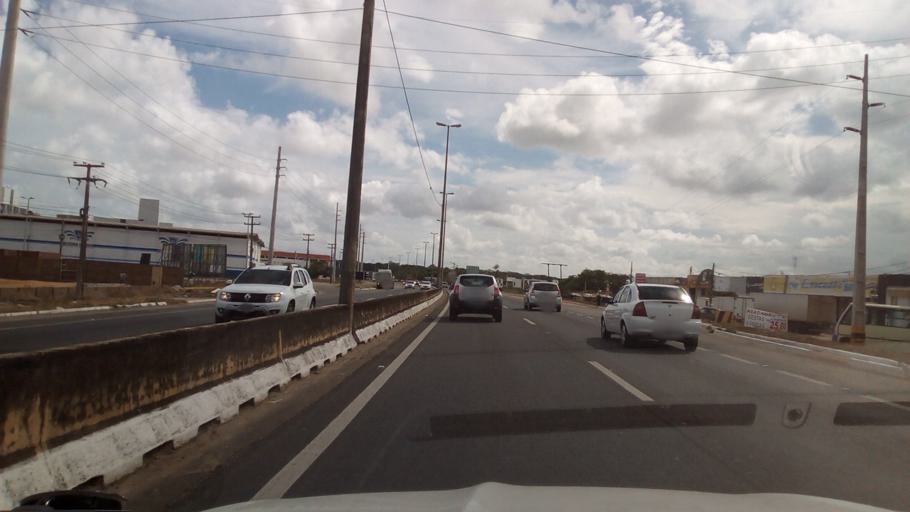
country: BR
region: Paraiba
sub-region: Joao Pessoa
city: Joao Pessoa
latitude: -7.0502
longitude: -34.8495
